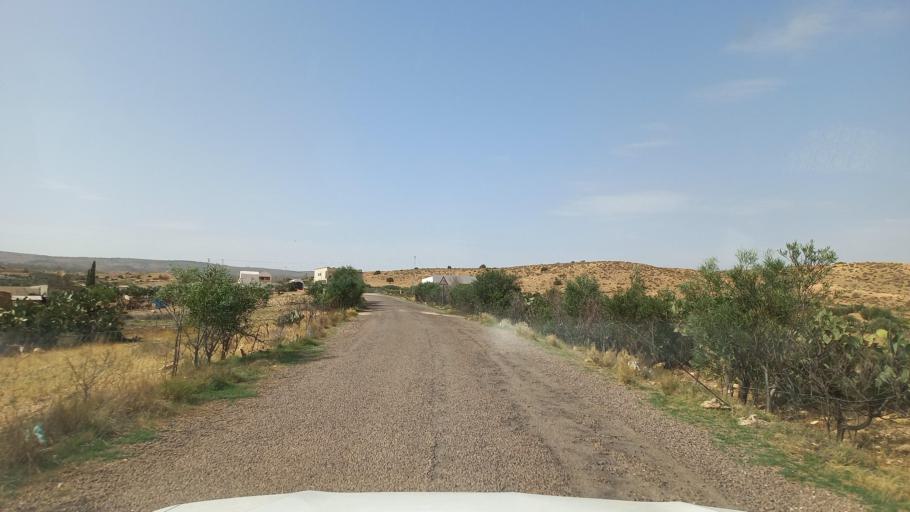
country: TN
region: Al Qasrayn
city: Kasserine
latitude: 35.3019
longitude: 8.9504
